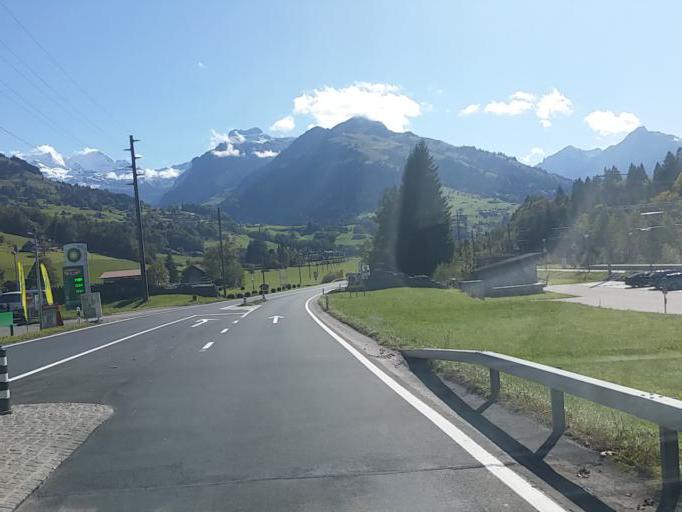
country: CH
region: Bern
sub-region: Frutigen-Niedersimmental District
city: Aeschi
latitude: 46.6383
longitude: 7.6917
